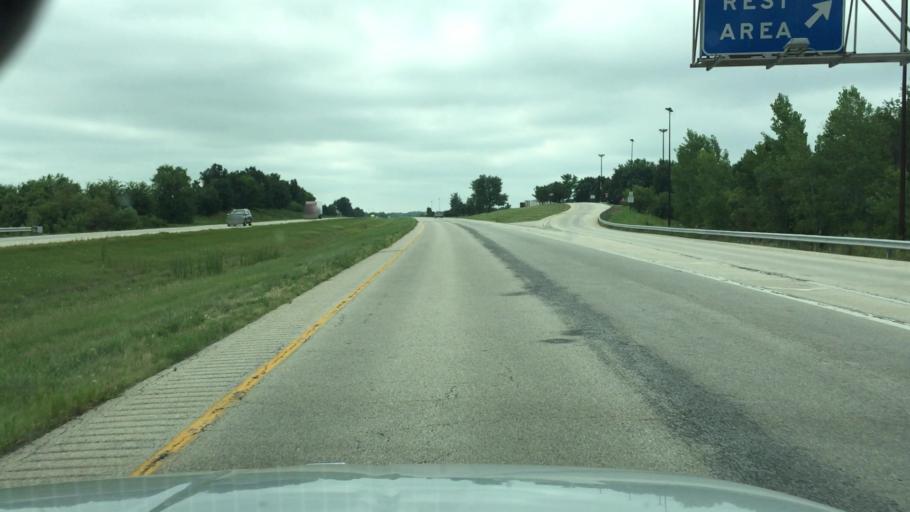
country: US
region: Illinois
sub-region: Henry County
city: Orion
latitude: 41.2369
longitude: -90.3320
